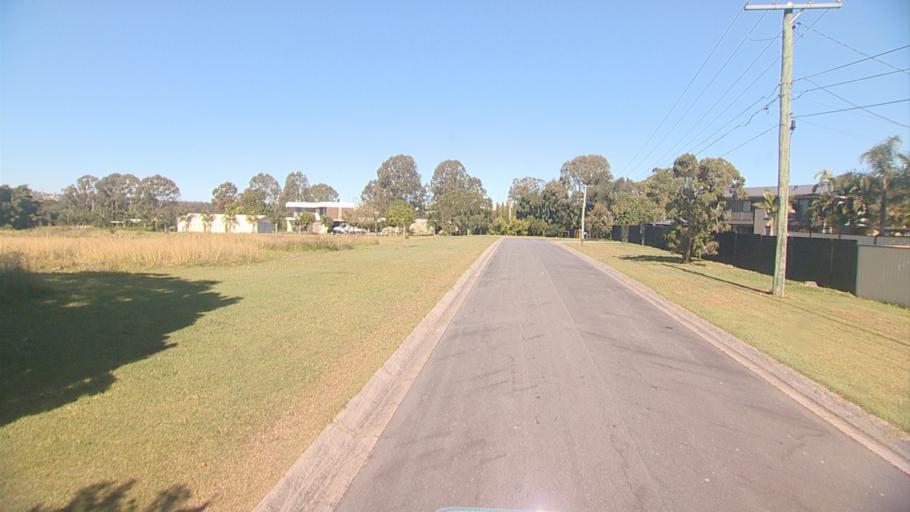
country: AU
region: Queensland
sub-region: Logan
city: Waterford West
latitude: -27.6886
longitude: 153.1421
